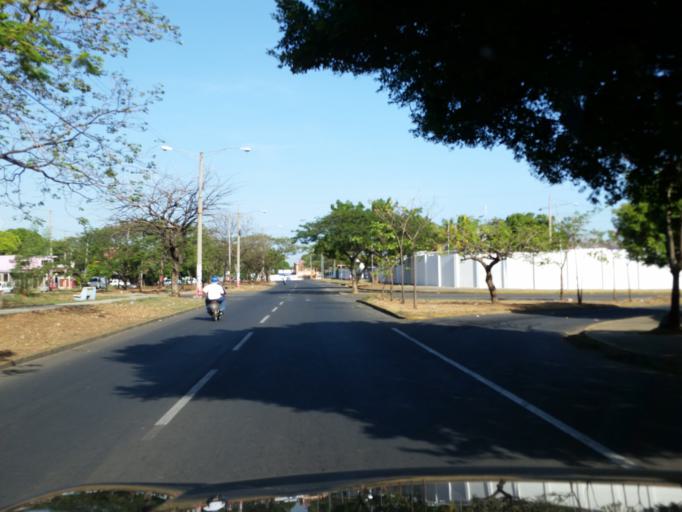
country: NI
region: Managua
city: Managua
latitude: 12.1556
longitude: -86.2847
